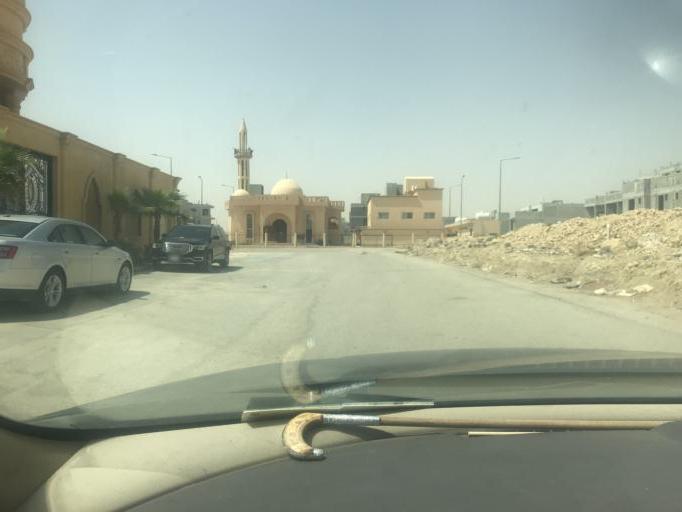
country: SA
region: Ar Riyad
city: Riyadh
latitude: 24.7858
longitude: 46.5848
